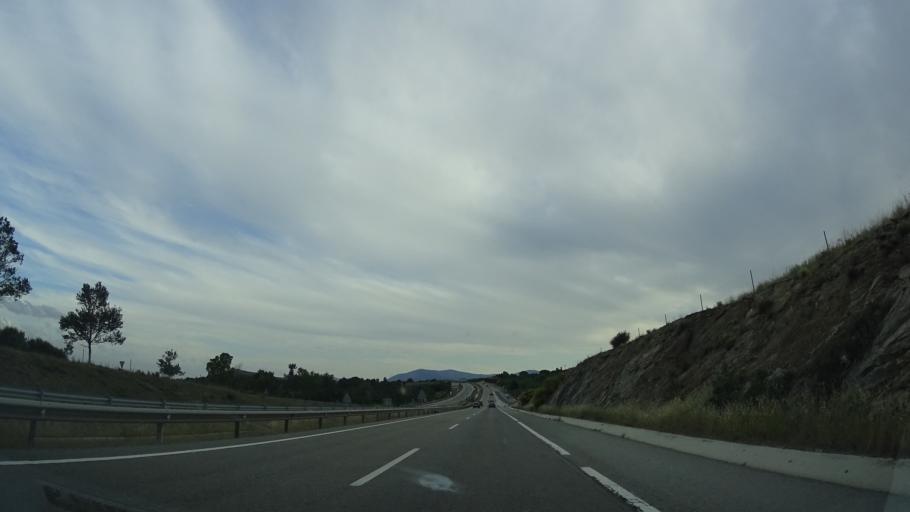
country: ES
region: Madrid
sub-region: Provincia de Madrid
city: Horcajo de la Sierra
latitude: 41.0616
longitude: -3.6106
